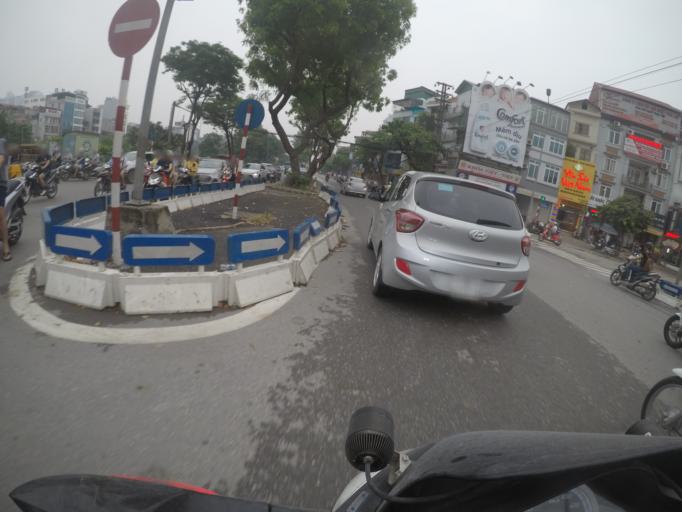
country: VN
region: Ha Noi
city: Dong Da
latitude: 21.0088
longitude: 105.8144
